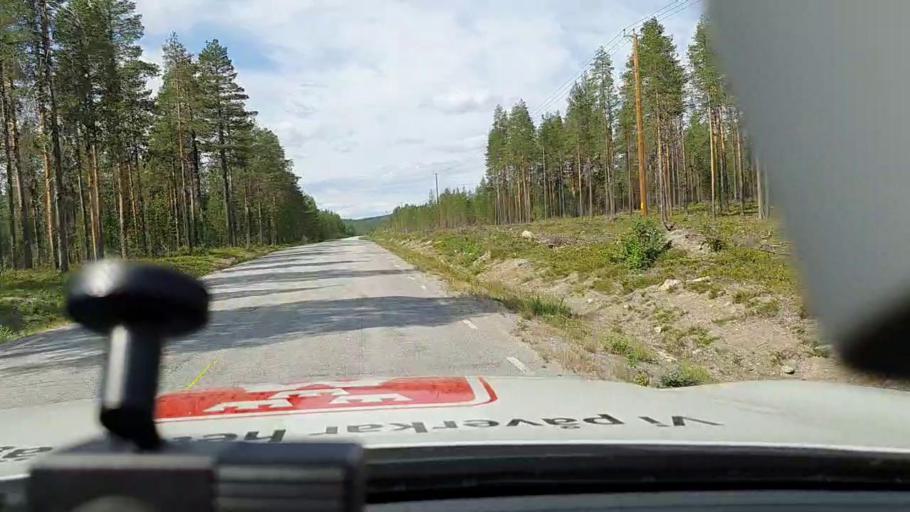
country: SE
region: Norrbotten
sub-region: Jokkmokks Kommun
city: Jokkmokk
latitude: 66.6233
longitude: 19.6821
